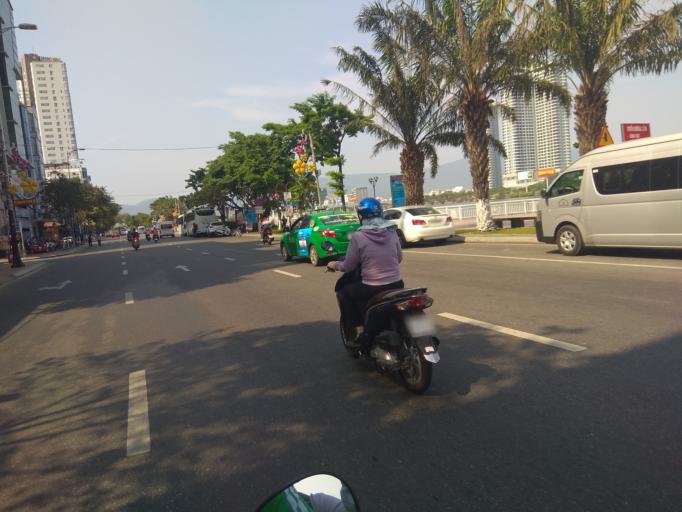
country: VN
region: Da Nang
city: Da Nang
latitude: 16.0669
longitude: 108.2249
